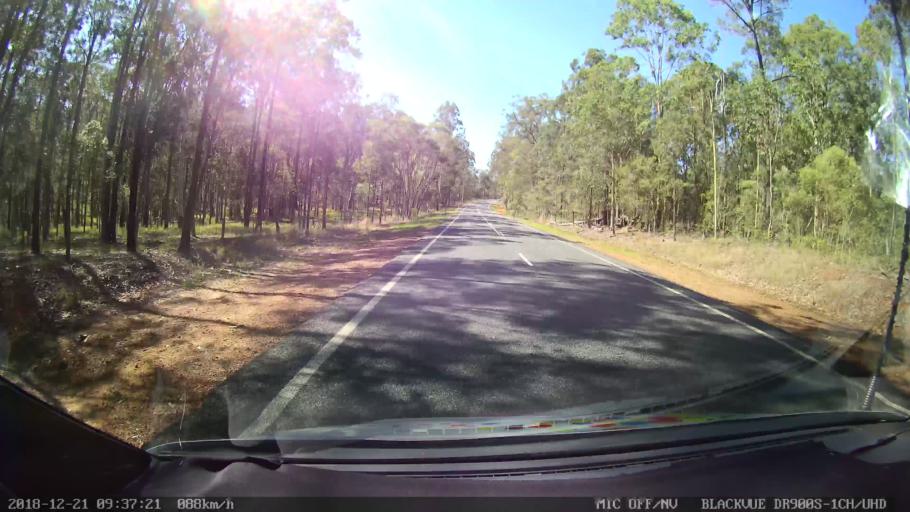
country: AU
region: New South Wales
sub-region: Clarence Valley
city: Grafton
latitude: -29.5351
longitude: 152.9863
